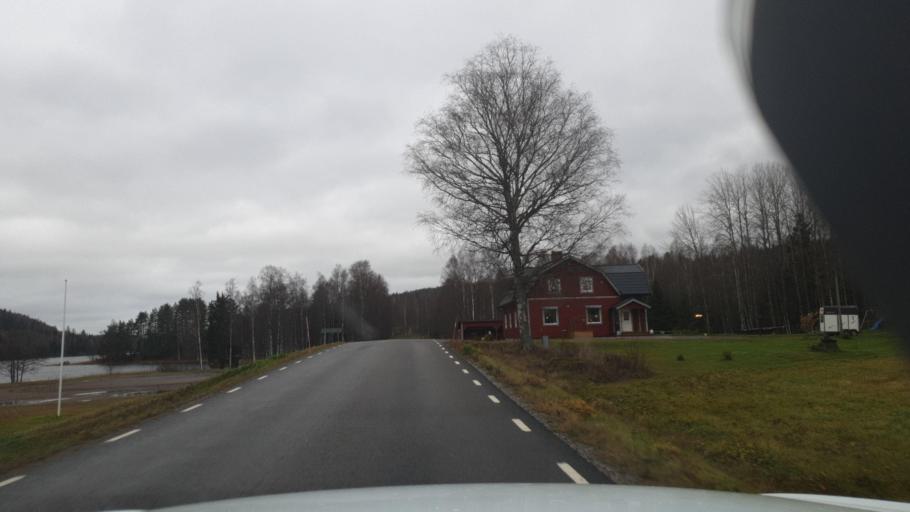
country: SE
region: Vaermland
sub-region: Eda Kommun
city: Amotfors
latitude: 59.8881
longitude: 12.5244
